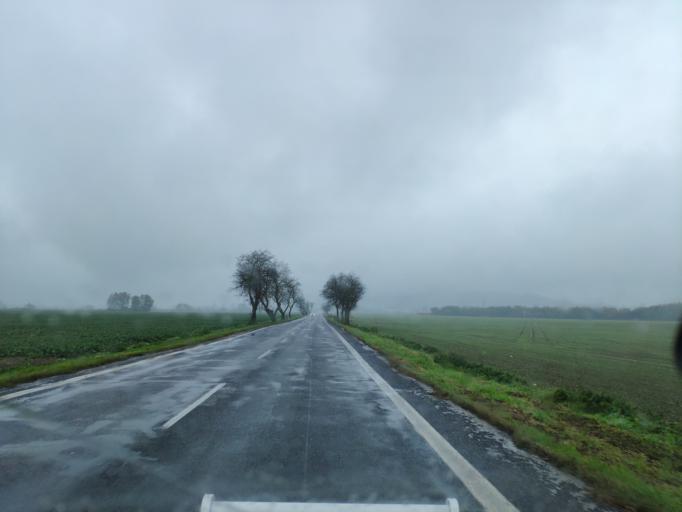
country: SK
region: Kosicky
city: Cierna nad Tisou
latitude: 48.4437
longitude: 21.9876
